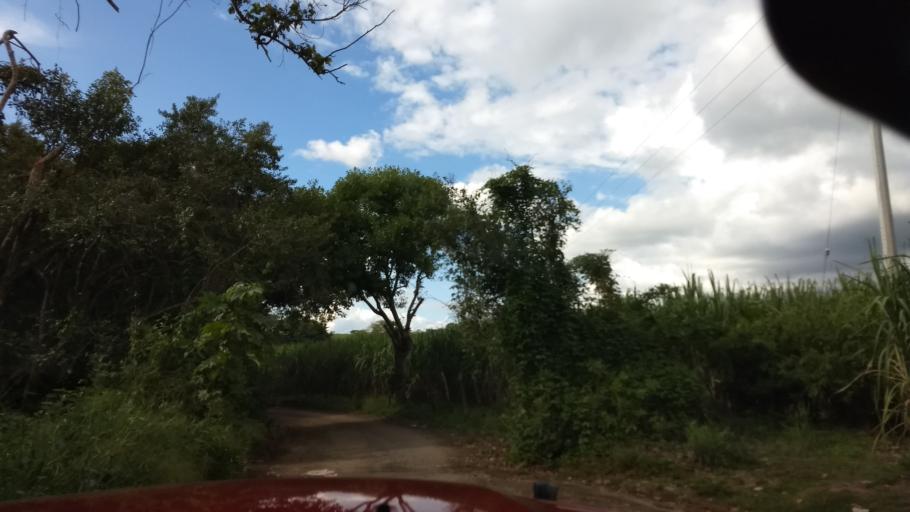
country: MX
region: Colima
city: Suchitlan
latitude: 19.4653
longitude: -103.7518
